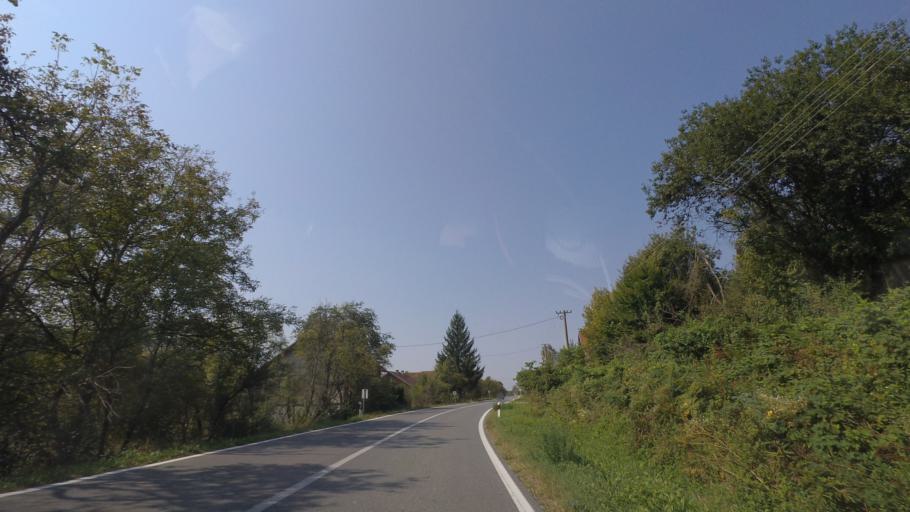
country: HR
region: Pozesko-Slavonska
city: Pakrac
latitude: 45.4629
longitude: 17.2383
